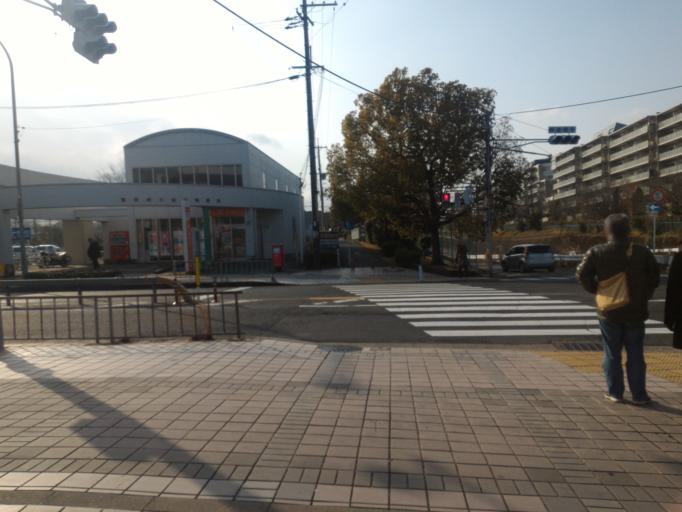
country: JP
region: Osaka
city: Tondabayashicho
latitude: 34.5009
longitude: 135.5789
